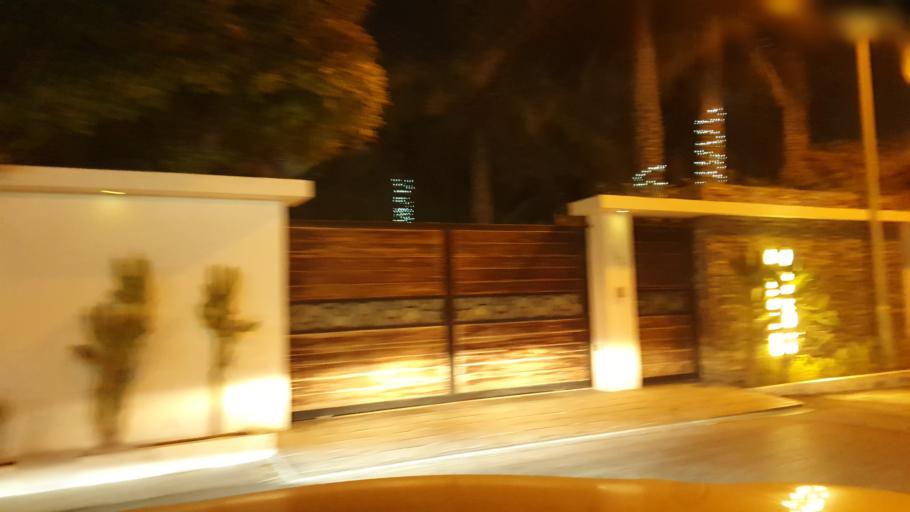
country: BH
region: Manama
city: Jidd Hafs
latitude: 26.1978
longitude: 50.4947
